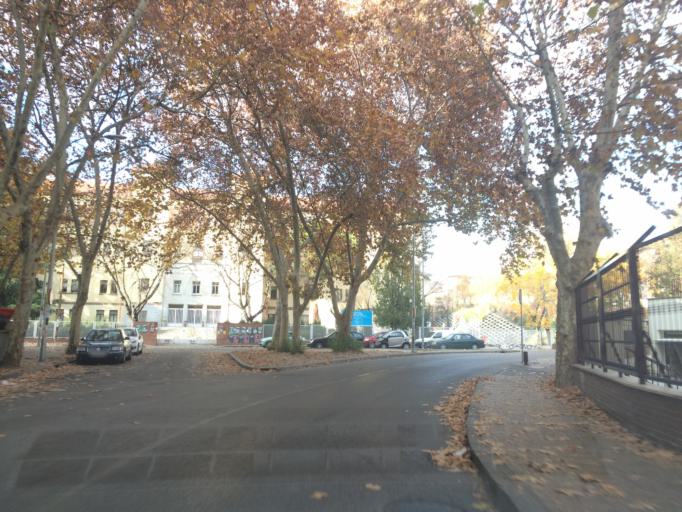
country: ES
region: Madrid
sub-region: Provincia de Madrid
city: Tetuan de las Victorias
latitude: 40.4496
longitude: -3.7170
